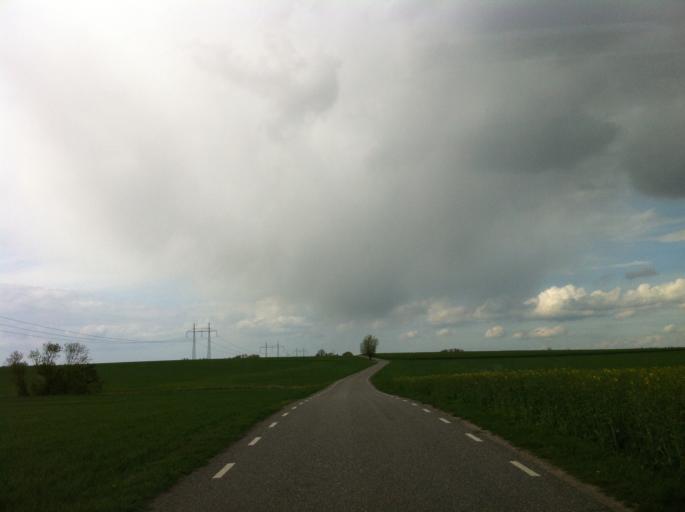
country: SE
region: Skane
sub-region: Svalovs Kommun
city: Teckomatorp
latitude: 55.8476
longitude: 13.0678
